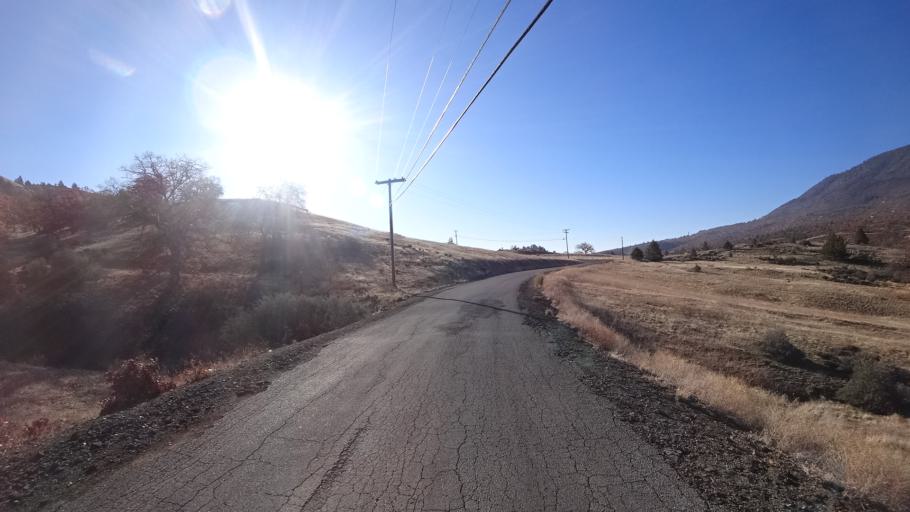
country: US
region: California
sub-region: Siskiyou County
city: Montague
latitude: 41.8868
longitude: -122.4748
